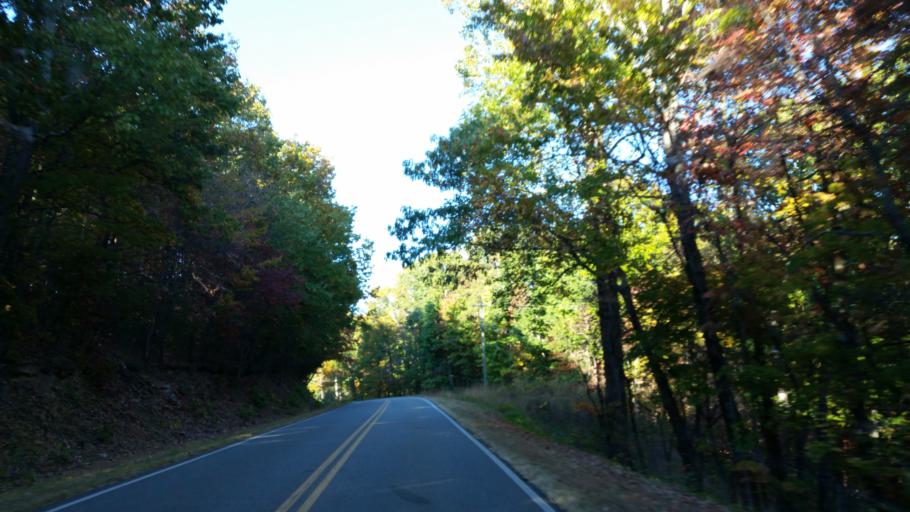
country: US
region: Georgia
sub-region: Gilmer County
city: Ellijay
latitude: 34.5909
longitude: -84.4582
